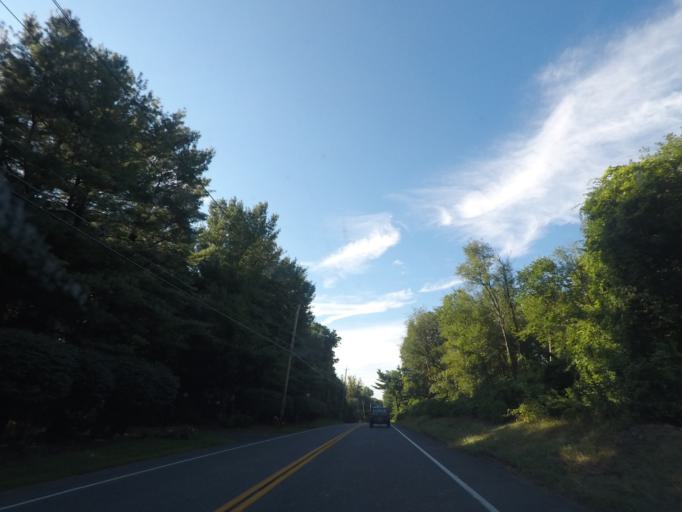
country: US
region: New York
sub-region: Albany County
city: West Albany
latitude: 42.7116
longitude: -73.7616
